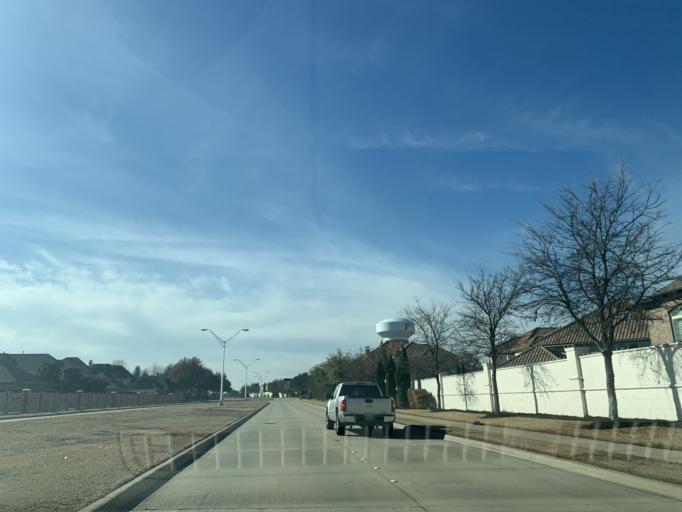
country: US
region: Texas
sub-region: Denton County
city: The Colony
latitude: 33.0568
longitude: -96.8170
